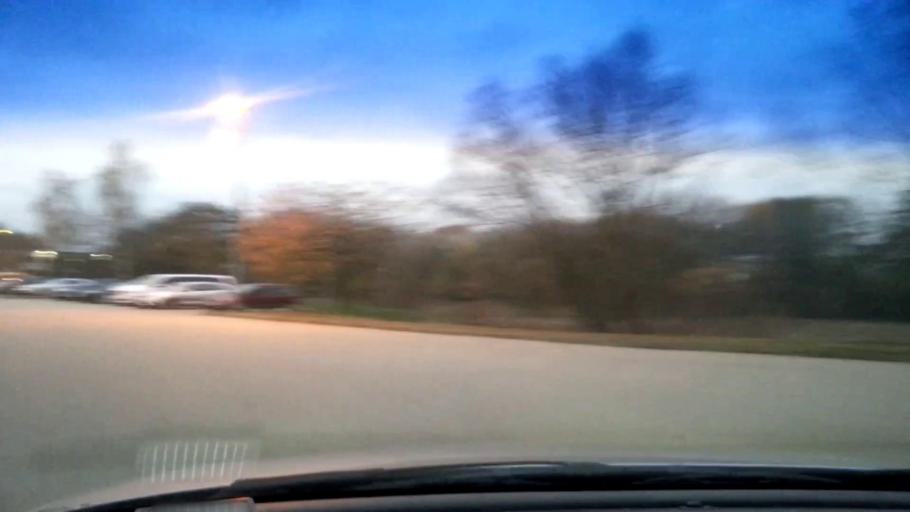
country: DE
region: Bavaria
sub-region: Upper Franconia
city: Gundelsheim
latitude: 49.9204
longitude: 10.9218
